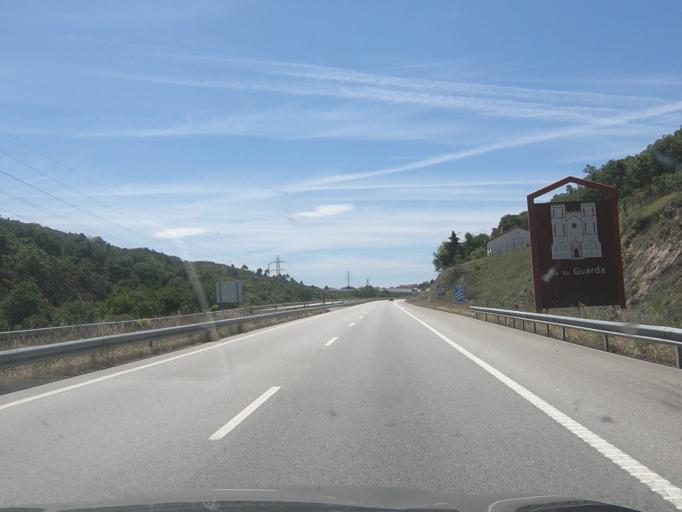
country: PT
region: Guarda
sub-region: Guarda
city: Sequeira
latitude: 40.5771
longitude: -7.2514
